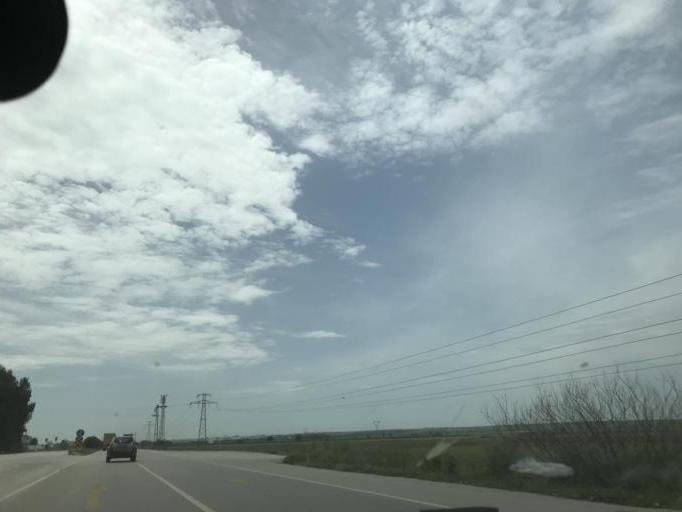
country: TR
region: Adana
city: Ceyhan
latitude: 37.0246
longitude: 35.7288
